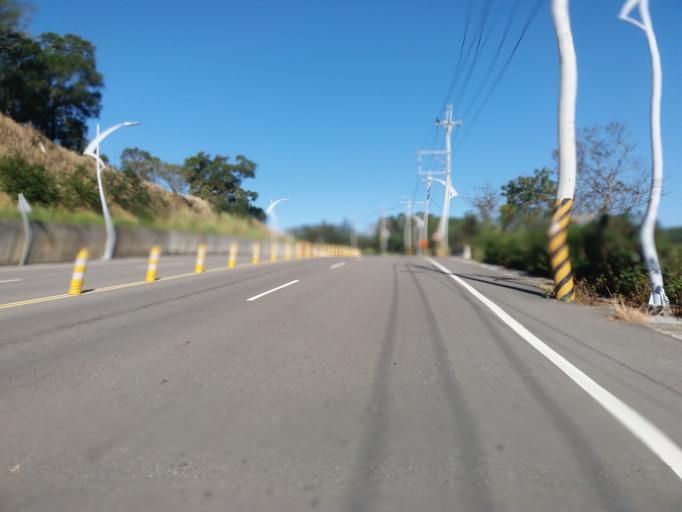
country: TW
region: Taiwan
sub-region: Hsinchu
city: Hsinchu
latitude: 24.7455
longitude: 120.9581
